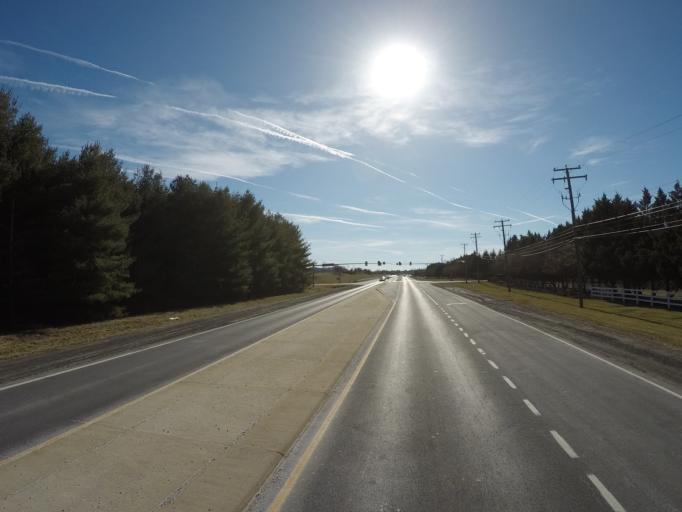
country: US
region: Virginia
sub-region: Loudoun County
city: Leesburg
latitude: 39.1541
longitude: -77.5397
